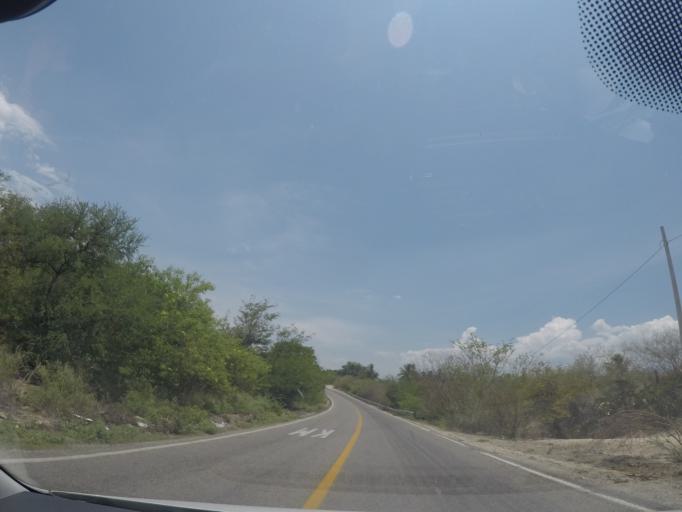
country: MX
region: Oaxaca
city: Santa Maria Jalapa del Marques
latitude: 16.4386
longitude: -95.5220
